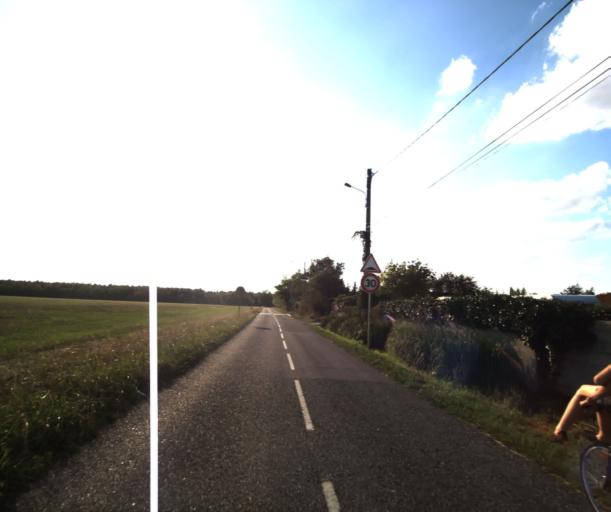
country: FR
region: Midi-Pyrenees
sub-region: Departement de la Haute-Garonne
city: Labastidette
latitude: 43.4779
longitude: 1.2544
